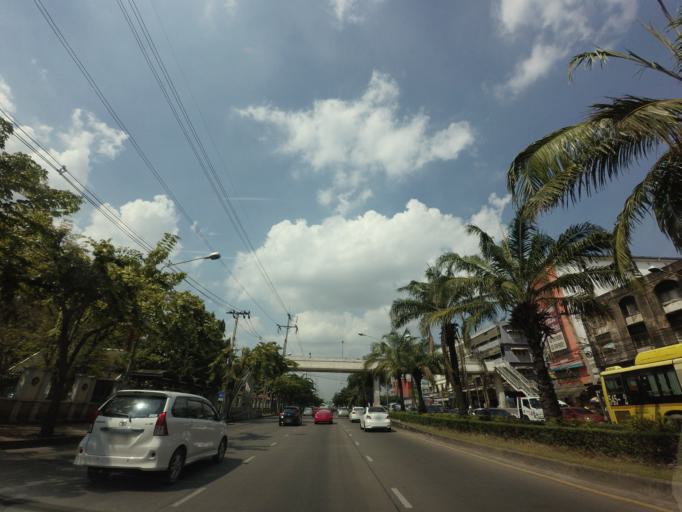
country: TH
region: Bangkok
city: Chatuchak
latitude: 13.8509
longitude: 100.5553
